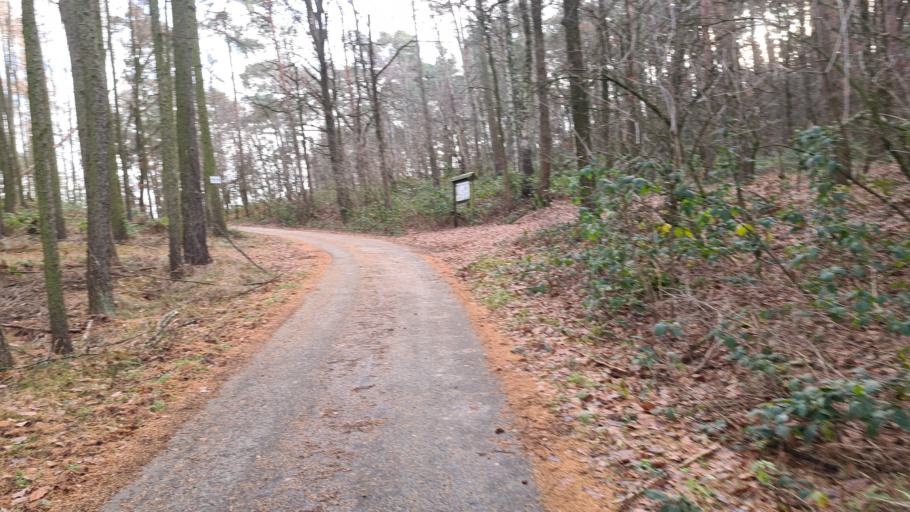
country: DE
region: Brandenburg
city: Groden
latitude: 51.3905
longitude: 13.5852
